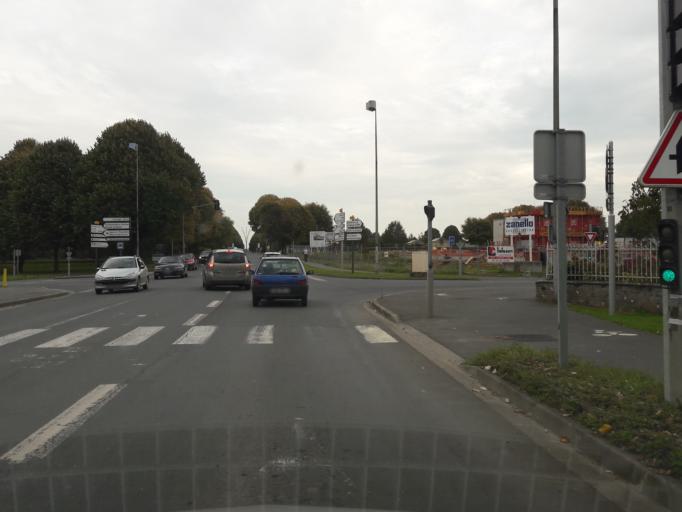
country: FR
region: Lower Normandy
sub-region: Departement du Calvados
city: Bayeux
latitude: 49.2758
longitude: -0.7164
